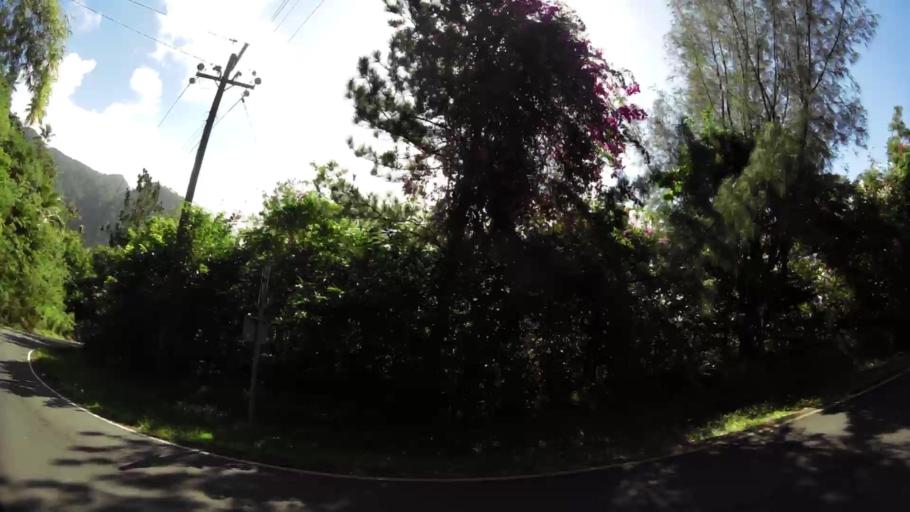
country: LC
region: Soufriere
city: Soufriere
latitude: 13.8638
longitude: -61.0540
